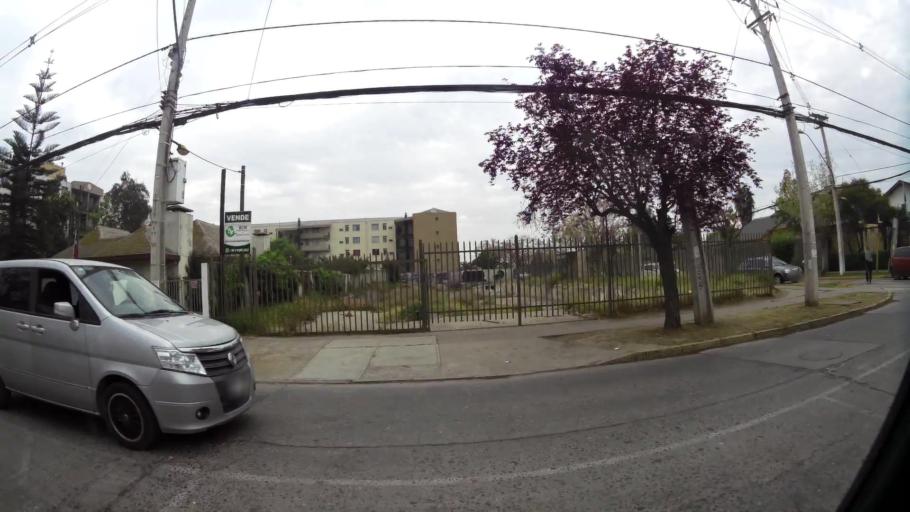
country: CL
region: Santiago Metropolitan
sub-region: Provincia de Santiago
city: Lo Prado
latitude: -33.5056
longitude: -70.7554
